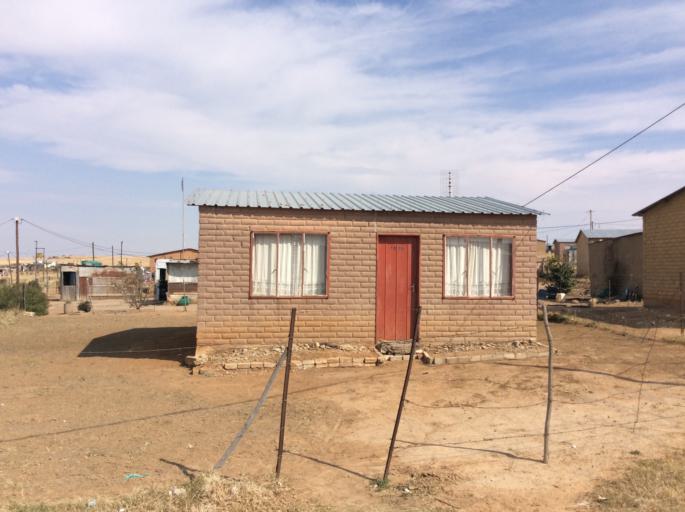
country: ZA
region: Orange Free State
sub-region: Xhariep District Municipality
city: Dewetsdorp
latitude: -29.5973
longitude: 26.6817
